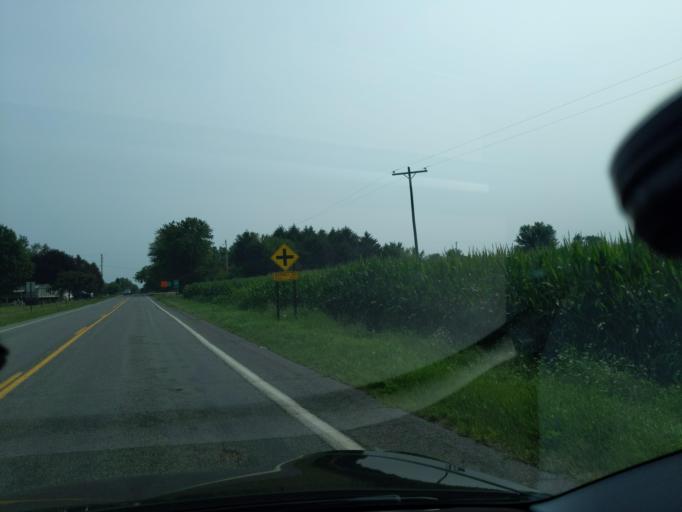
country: US
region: Michigan
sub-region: Eaton County
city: Eaton Rapids
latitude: 42.5258
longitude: -84.5619
